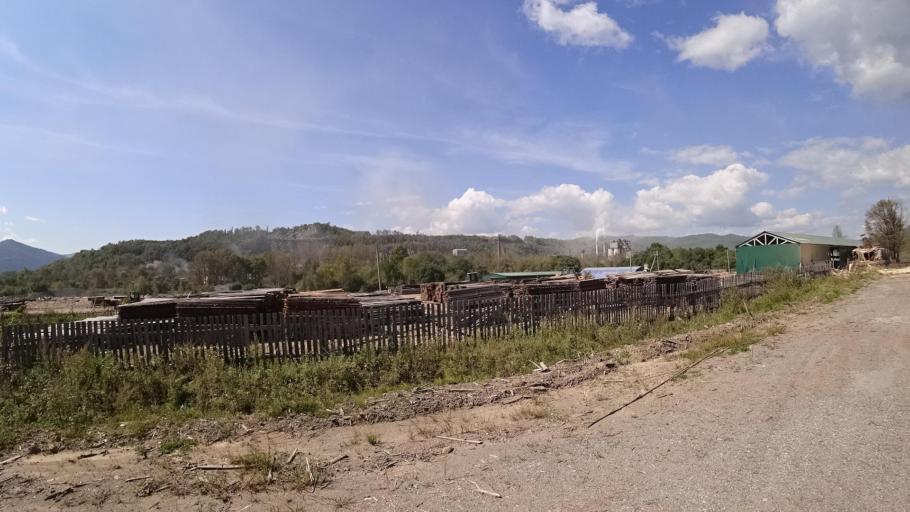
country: RU
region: Jewish Autonomous Oblast
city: Londoko
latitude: 49.0114
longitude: 131.9418
